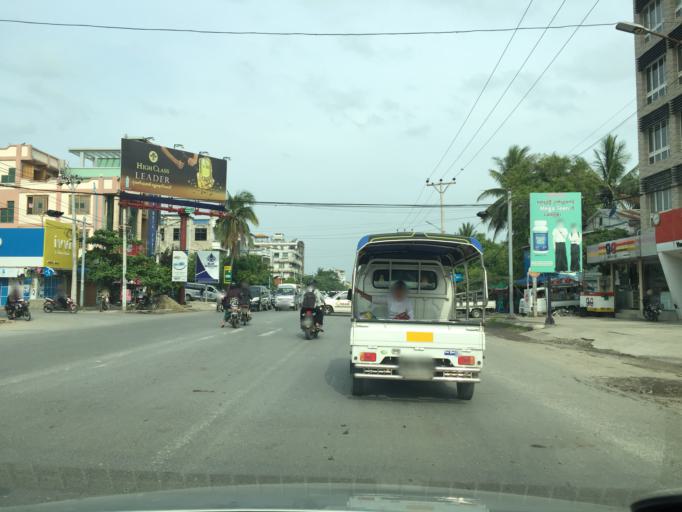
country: MM
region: Mandalay
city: Mandalay
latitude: 21.9681
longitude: 96.1017
